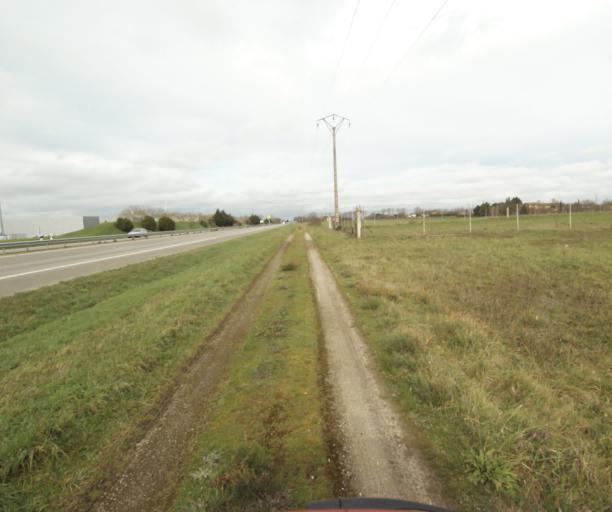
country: FR
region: Midi-Pyrenees
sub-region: Departement de l'Ariege
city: La Tour-du-Crieu
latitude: 43.1100
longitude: 1.6319
